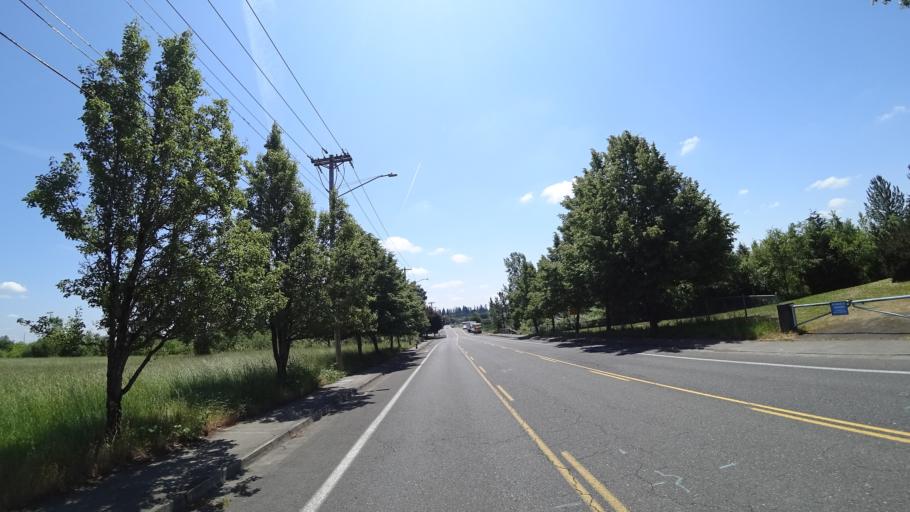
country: US
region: Oregon
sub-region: Multnomah County
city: Fairview
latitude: 45.5567
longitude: -122.5002
